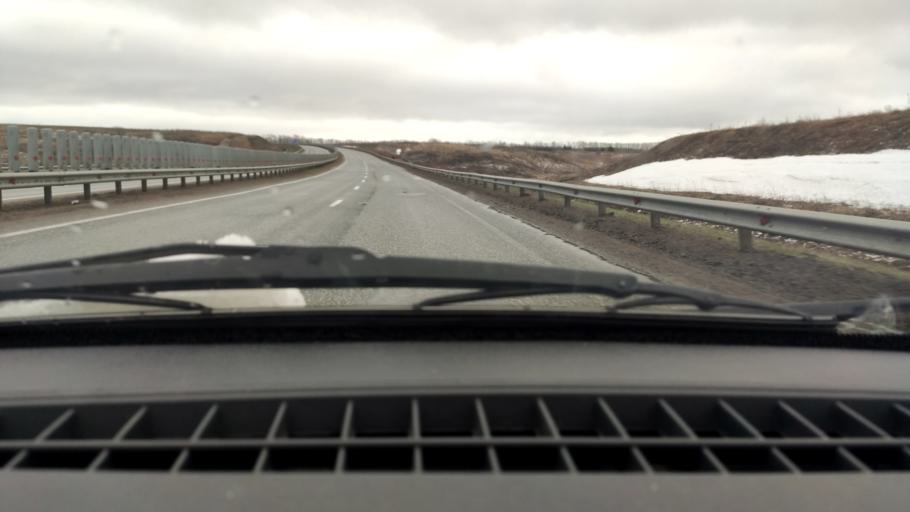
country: RU
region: Bashkortostan
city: Kushnarenkovo
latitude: 55.0677
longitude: 55.2992
